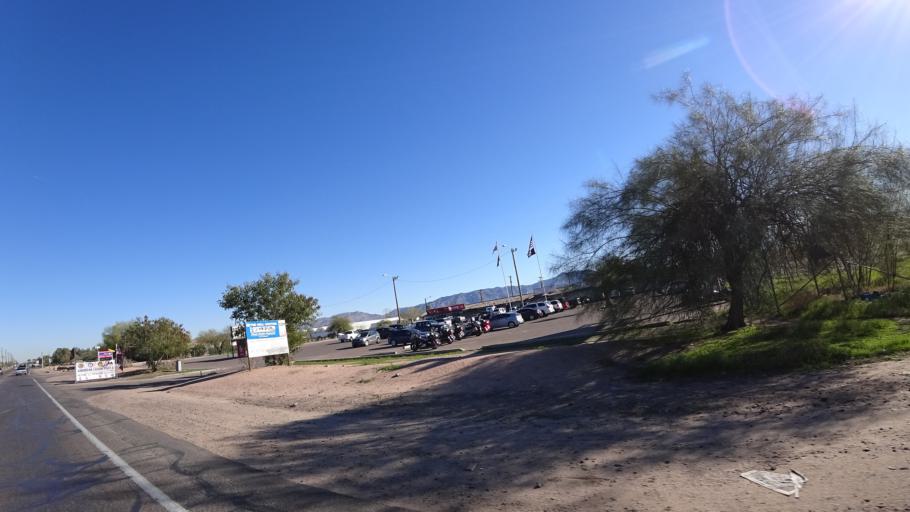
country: US
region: Arizona
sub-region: Maricopa County
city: Laveen
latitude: 33.3920
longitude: -112.1432
